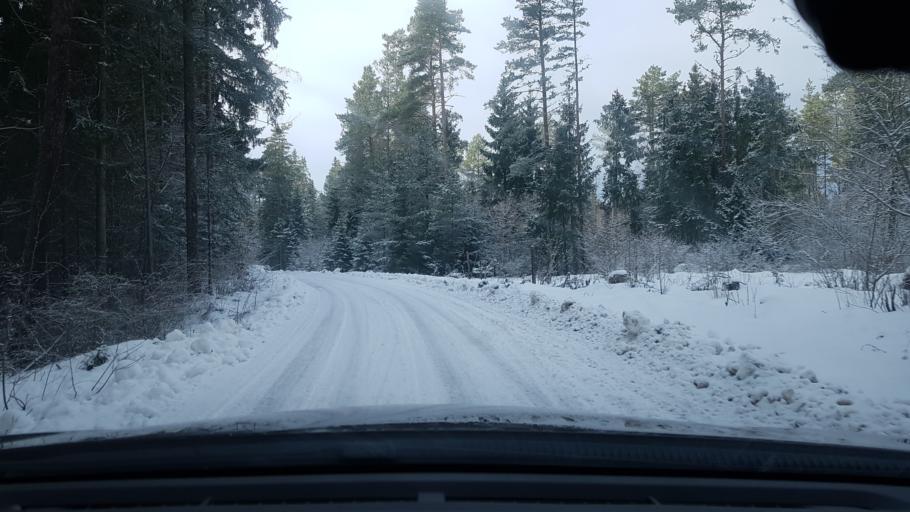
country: EE
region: Harju
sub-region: Keila linn
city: Keila
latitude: 59.2922
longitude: 24.2613
